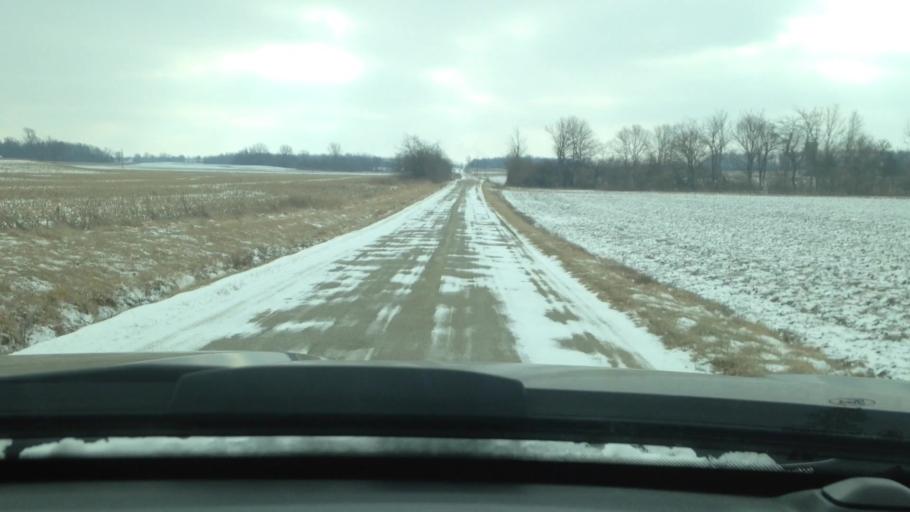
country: US
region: Indiana
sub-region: Randolph County
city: Union City
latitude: 40.2701
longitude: -84.8622
